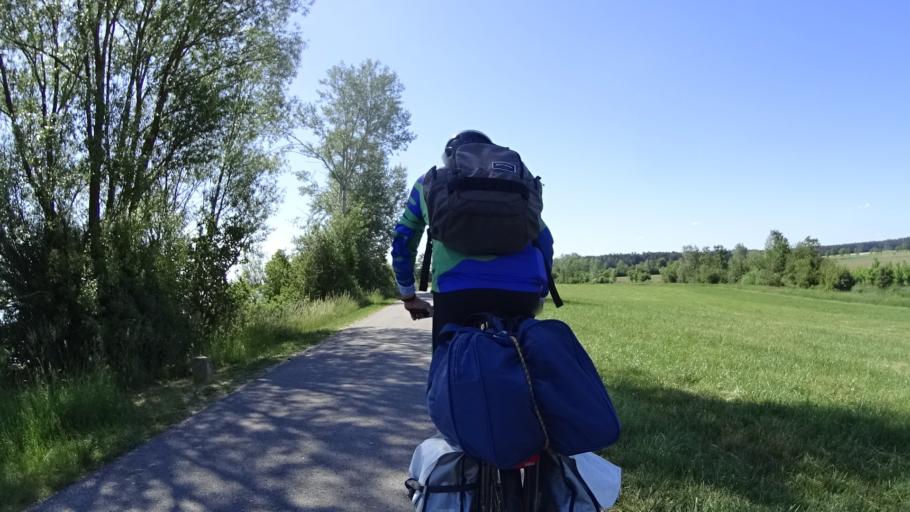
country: DE
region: Bavaria
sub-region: Regierungsbezirk Mittelfranken
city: Muhr am See
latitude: 49.1304
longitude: 10.7164
